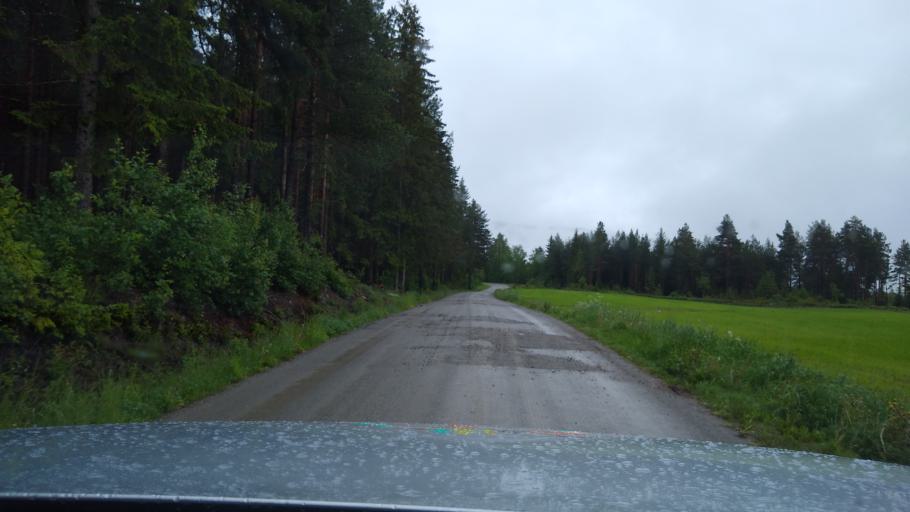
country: NO
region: Oppland
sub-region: Ringebu
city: Ringebu
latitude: 61.5398
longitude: 10.1166
